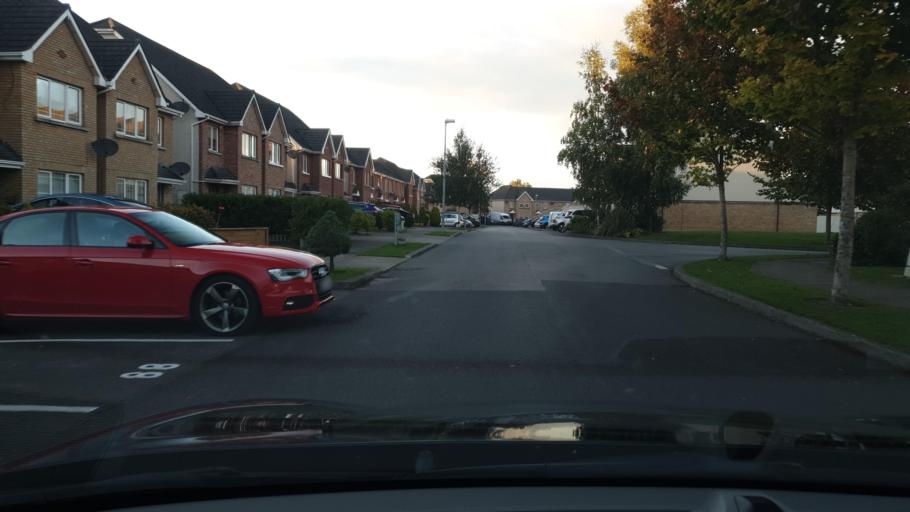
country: IE
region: Leinster
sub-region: An Mhi
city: Ashbourne
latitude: 53.5001
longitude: -6.3909
